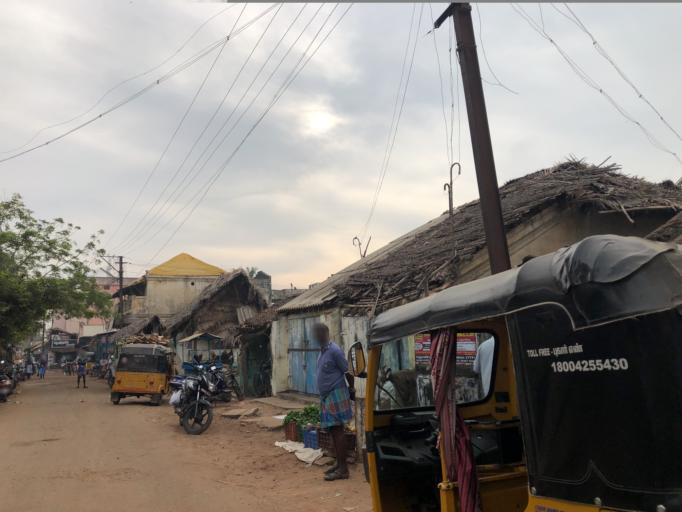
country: IN
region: Tamil Nadu
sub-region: Thanjavur
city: Adirampattinam
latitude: 10.3400
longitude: 79.3802
